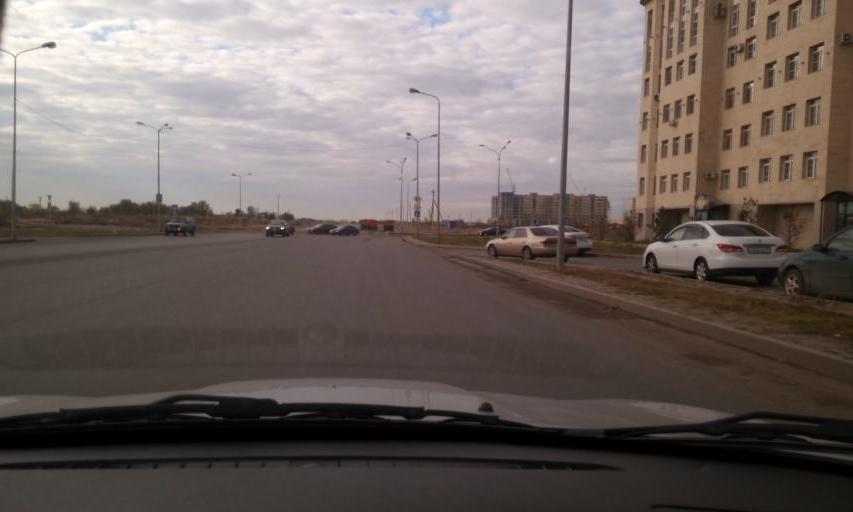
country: KZ
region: Astana Qalasy
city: Astana
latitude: 51.1231
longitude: 71.4863
